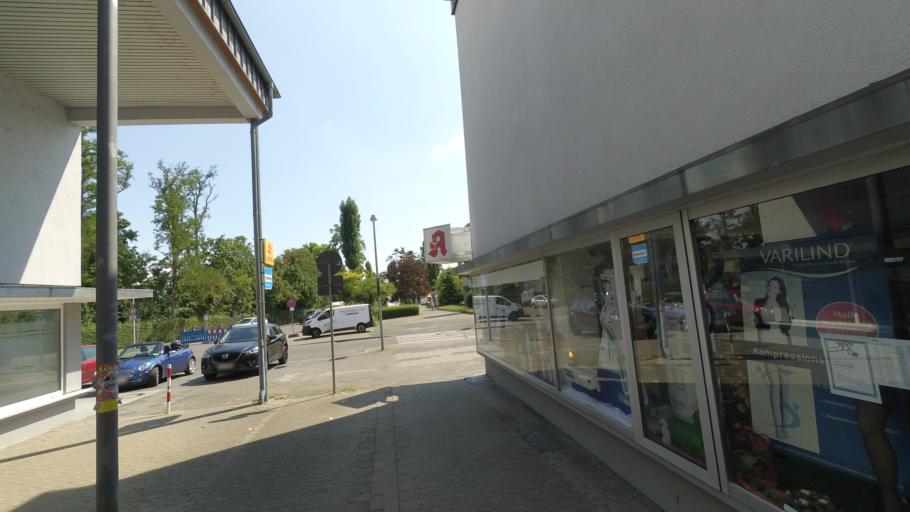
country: DE
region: Rheinland-Pfalz
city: Frankenthal
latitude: 49.5056
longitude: 8.3749
